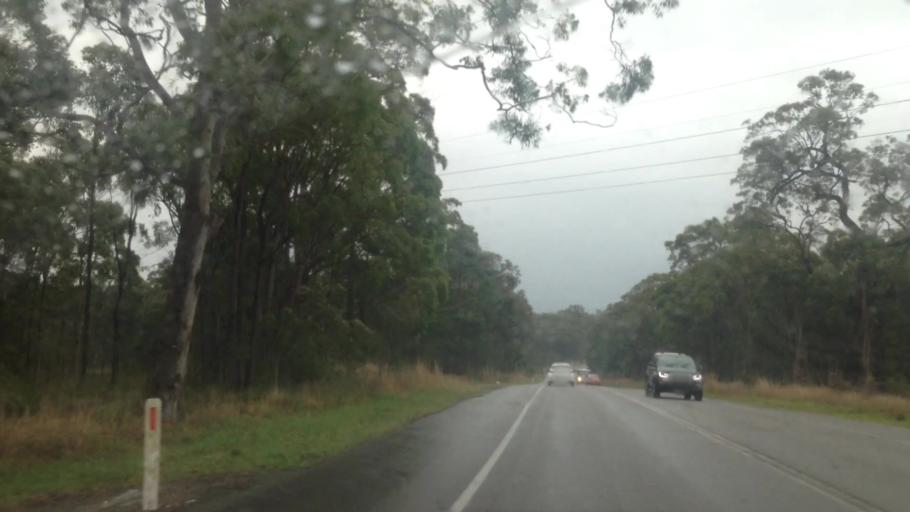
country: AU
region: New South Wales
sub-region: Lake Macquarie Shire
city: Dora Creek
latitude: -33.1291
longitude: 151.4763
